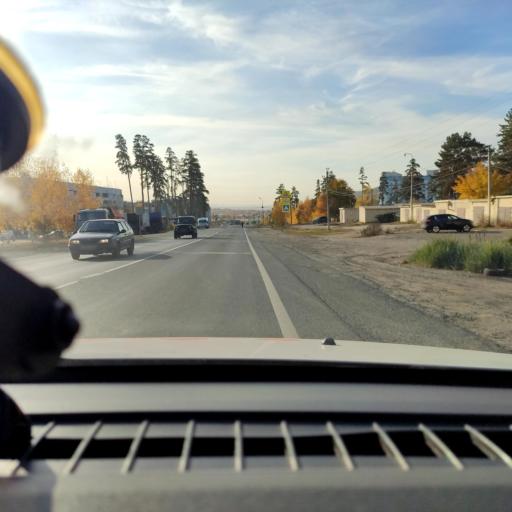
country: RU
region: Samara
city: Volzhskiy
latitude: 53.4394
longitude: 50.1241
